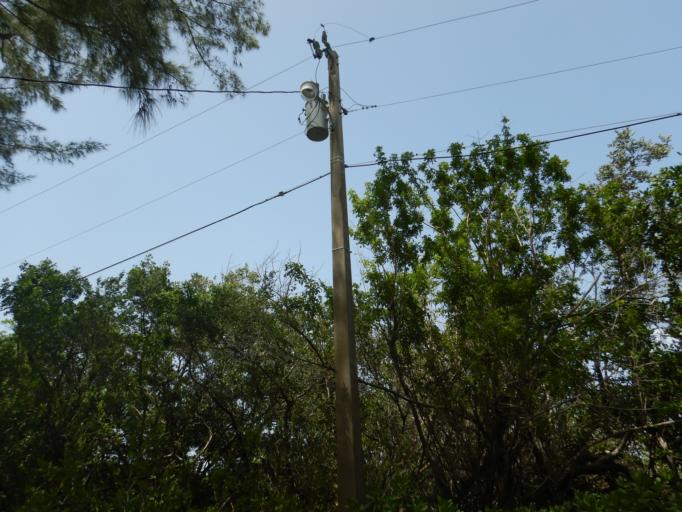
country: US
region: Florida
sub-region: Sarasota County
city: Vamo
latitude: 27.2268
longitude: -82.5207
